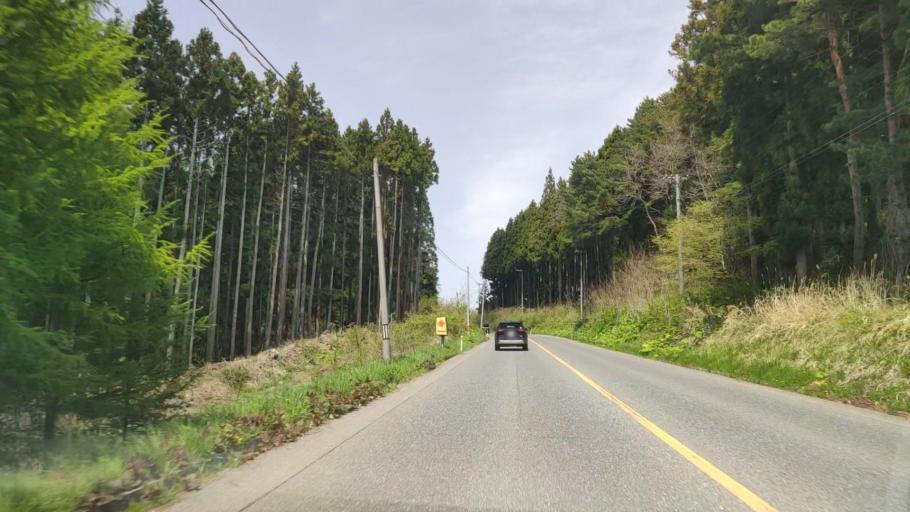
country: JP
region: Aomori
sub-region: Misawa Shi
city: Inuotose
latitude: 40.5648
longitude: 141.3811
